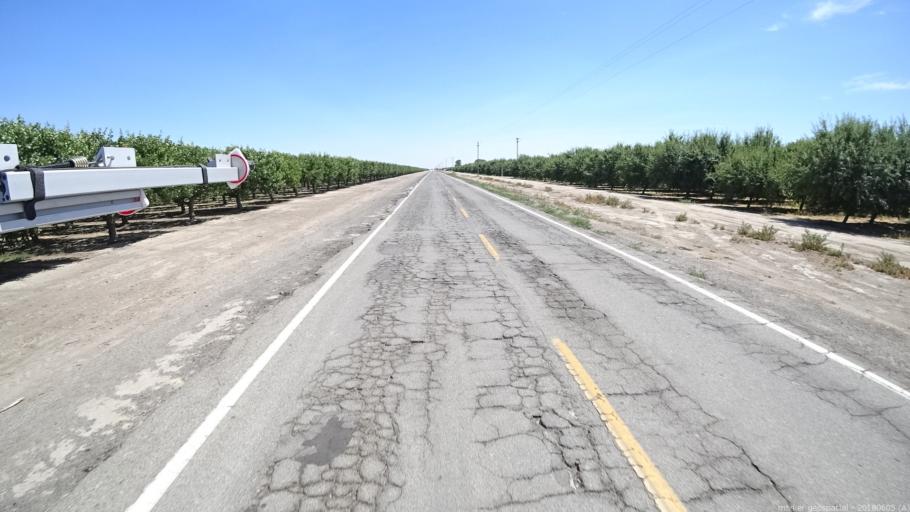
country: US
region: California
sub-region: Fresno County
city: Firebaugh
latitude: 36.9664
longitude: -120.3829
